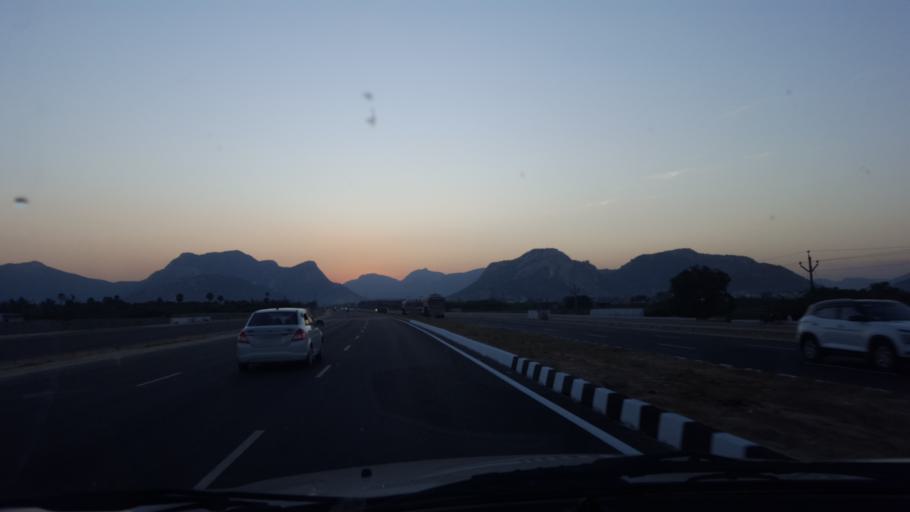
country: IN
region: Andhra Pradesh
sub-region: Chittoor
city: Narasingapuram
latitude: 13.5862
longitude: 79.3345
